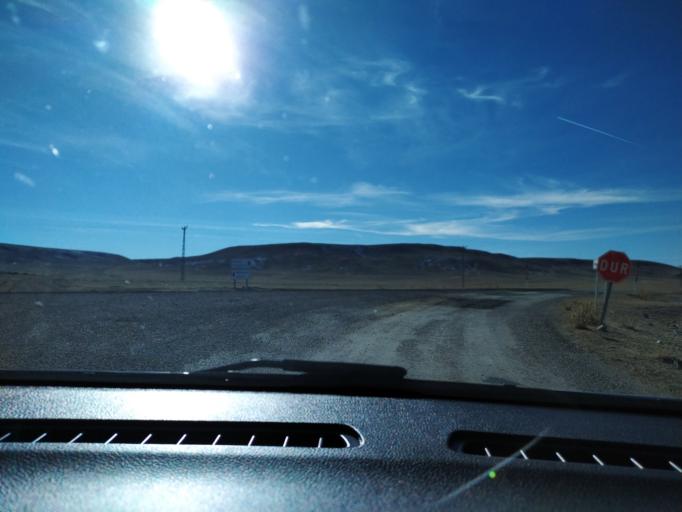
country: TR
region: Kayseri
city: Orensehir
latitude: 39.0976
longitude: 36.6981
